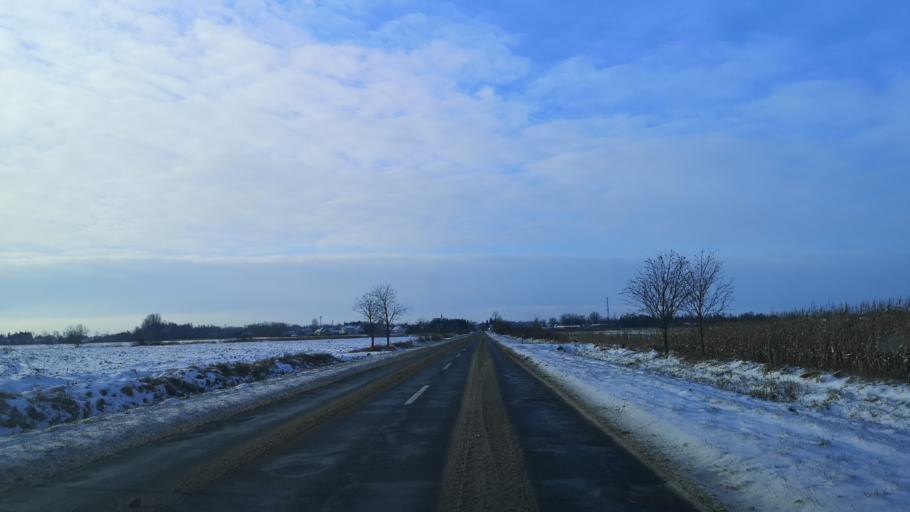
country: PL
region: Subcarpathian Voivodeship
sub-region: Powiat przeworski
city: Sieniawa
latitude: 50.1887
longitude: 22.6193
